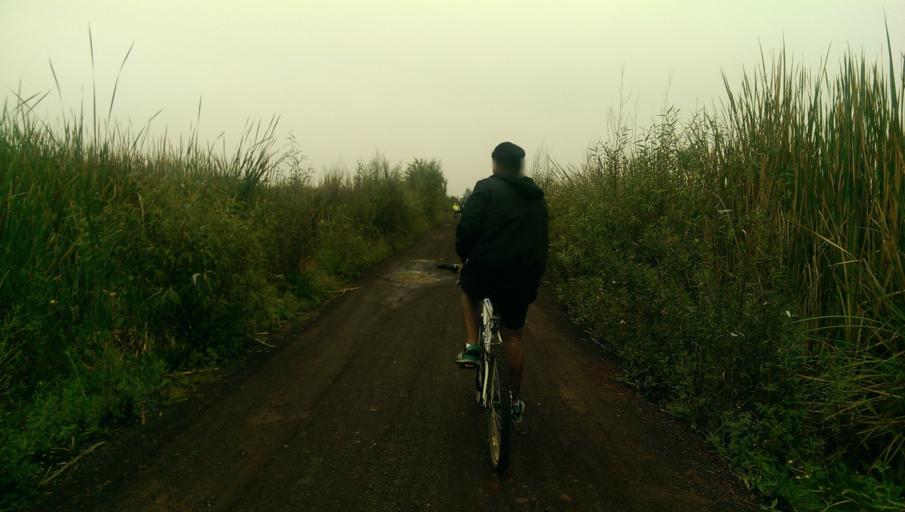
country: MX
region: Mexico City
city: Xochimilco
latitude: 19.2690
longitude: -99.0611
